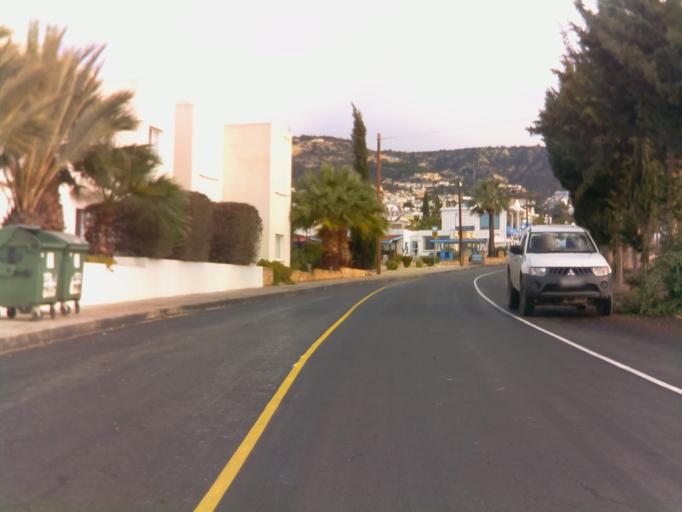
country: CY
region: Pafos
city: Pegeia
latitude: 34.8737
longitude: 32.3786
